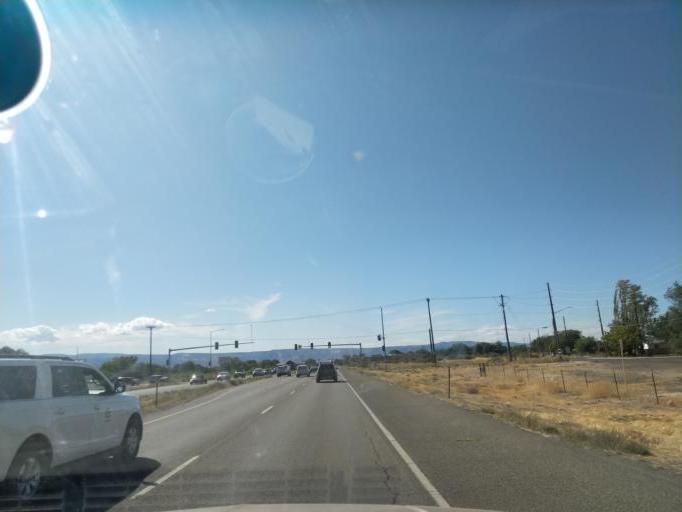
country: US
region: Colorado
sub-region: Mesa County
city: Clifton
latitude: 39.0844
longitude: -108.4674
